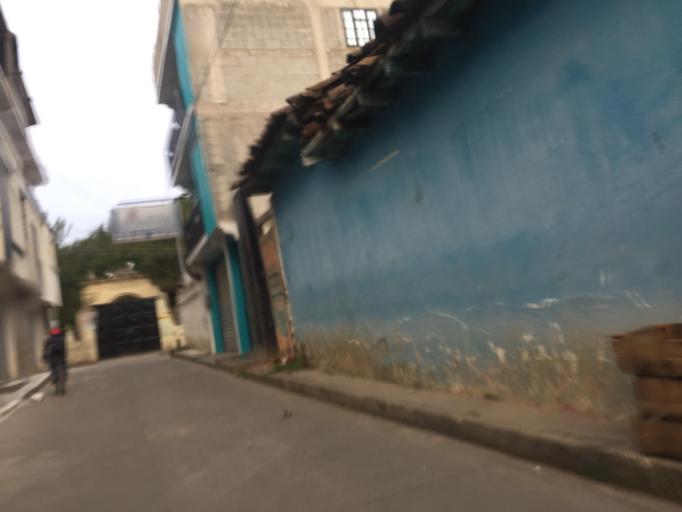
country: GT
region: Totonicapan
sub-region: Municipio de Totonicapan
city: Totonicapan
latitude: 14.9096
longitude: -91.3630
